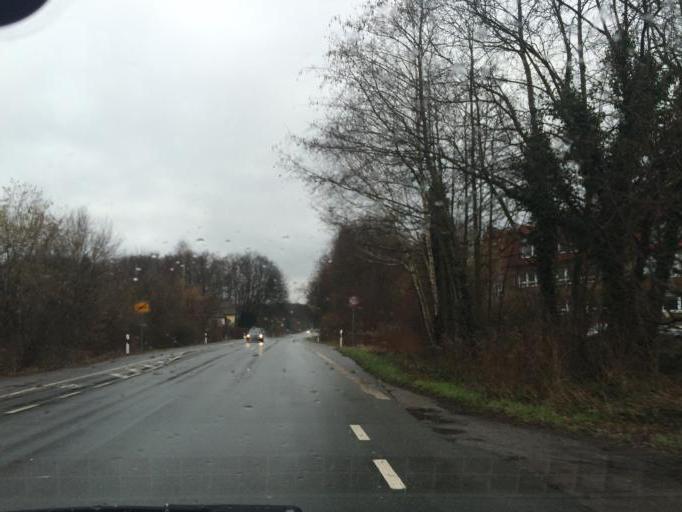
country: DE
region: North Rhine-Westphalia
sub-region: Regierungsbezirk Munster
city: Gladbeck
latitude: 51.5963
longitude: 6.9650
